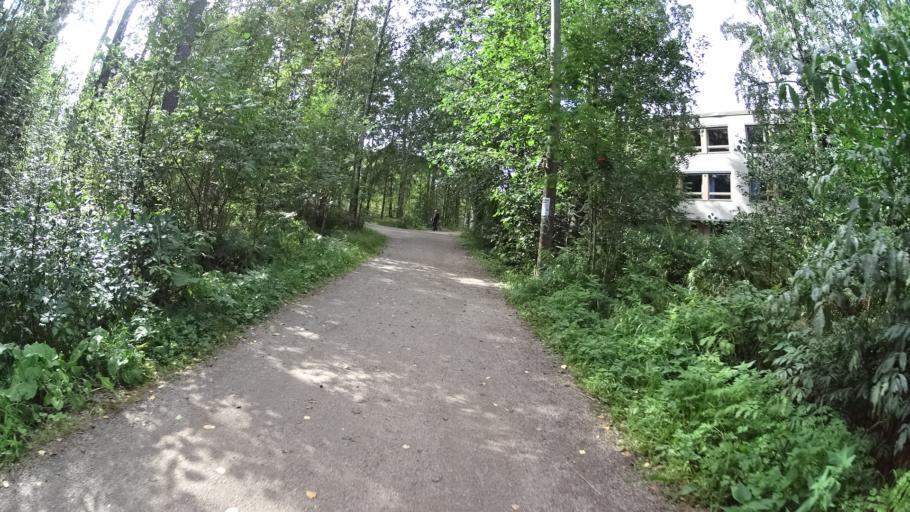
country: FI
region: Uusimaa
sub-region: Helsinki
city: Helsinki
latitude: 60.1965
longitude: 24.9090
